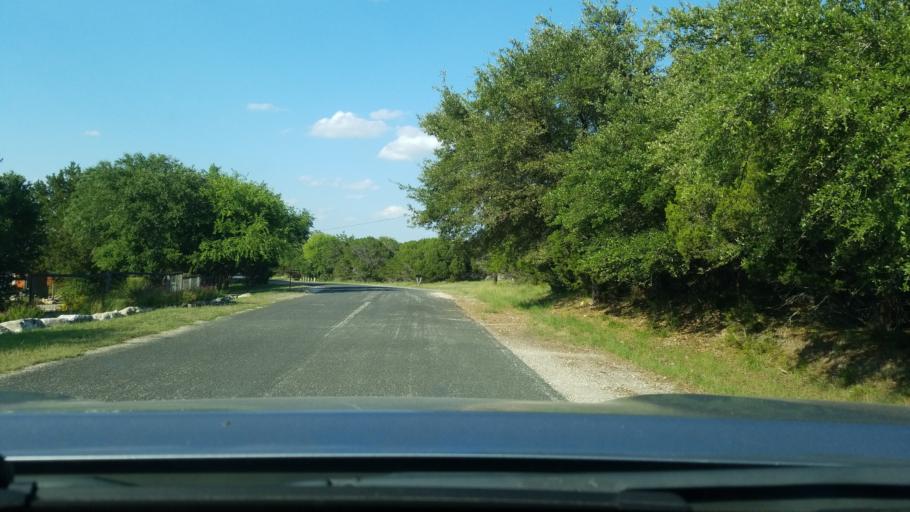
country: US
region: Texas
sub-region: Comal County
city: Bulverde
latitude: 29.7116
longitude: -98.4329
